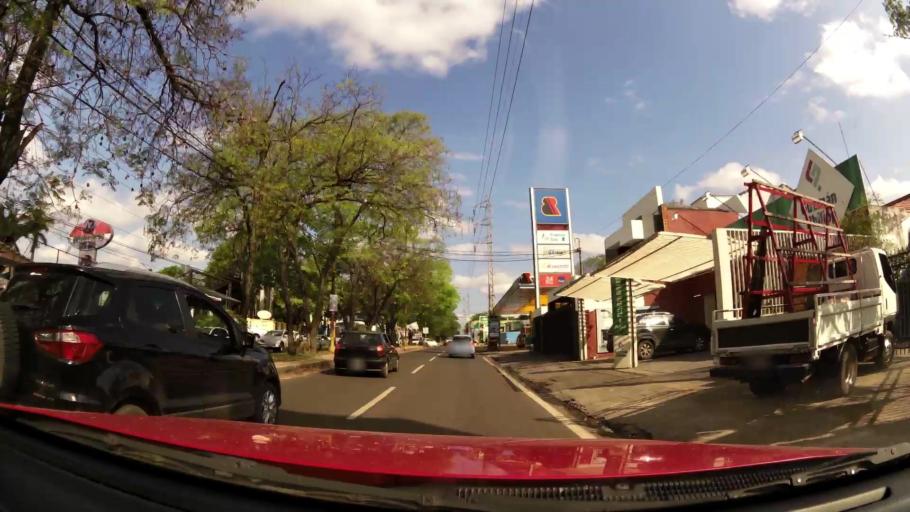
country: PY
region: Central
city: Fernando de la Mora
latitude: -25.3136
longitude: -57.5289
